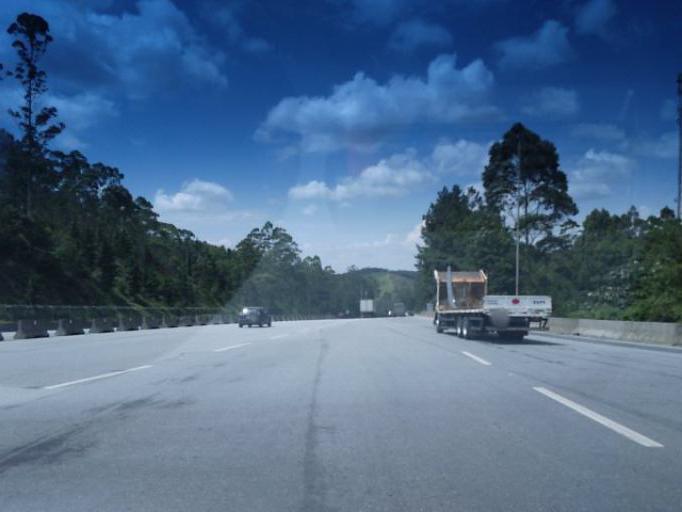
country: BR
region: Sao Paulo
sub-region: Sao Lourenco Da Serra
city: Sao Lourenco da Serra
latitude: -23.7895
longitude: -46.9145
